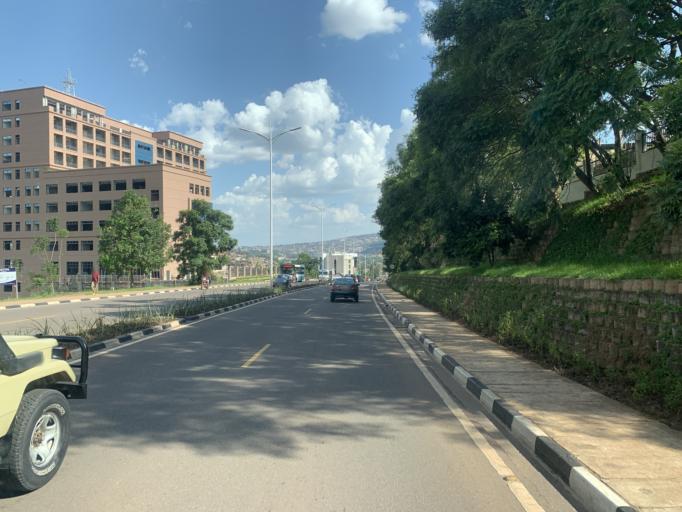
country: RW
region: Kigali
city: Kigali
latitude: -1.9491
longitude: 30.0718
